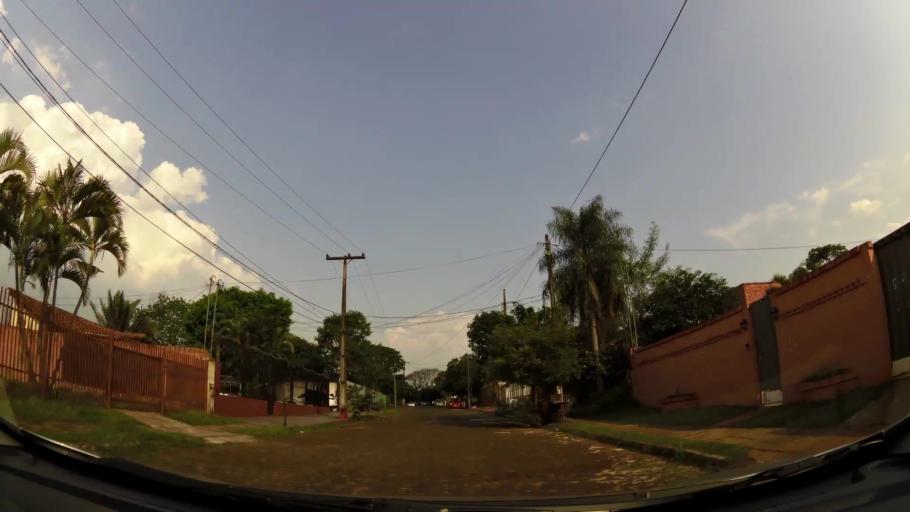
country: PY
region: Alto Parana
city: Presidente Franco
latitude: -25.5314
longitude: -54.6317
